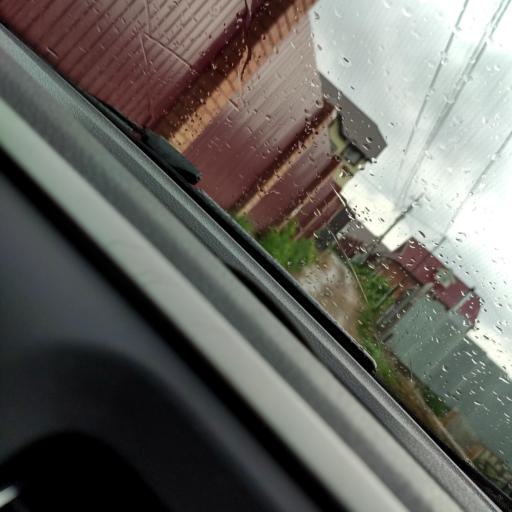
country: RU
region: Samara
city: Tol'yatti
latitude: 53.4730
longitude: 49.3691
